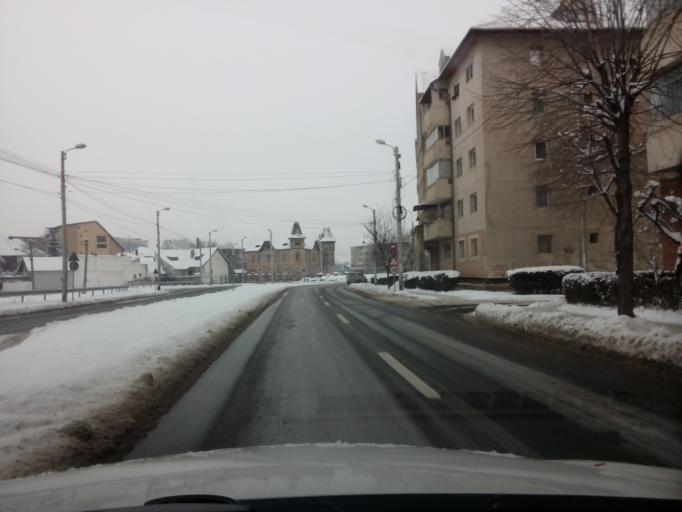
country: RO
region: Sibiu
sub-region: Municipiul Sibiu
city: Sibiu
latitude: 45.8004
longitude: 24.1571
